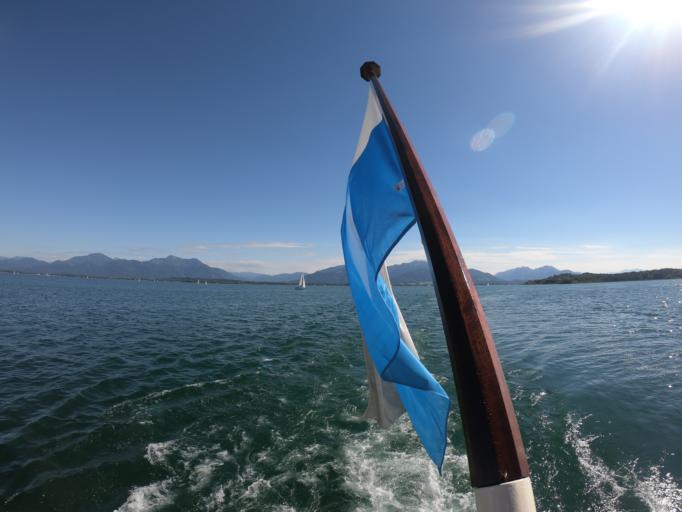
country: DE
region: Bavaria
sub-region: Upper Bavaria
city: Chiemsee
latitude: 47.8690
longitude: 12.4288
